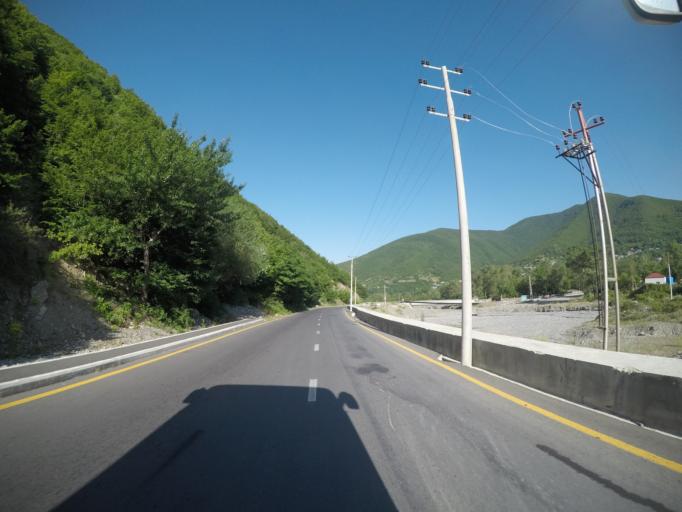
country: AZ
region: Shaki City
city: Sheki
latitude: 41.2418
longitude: 47.1903
